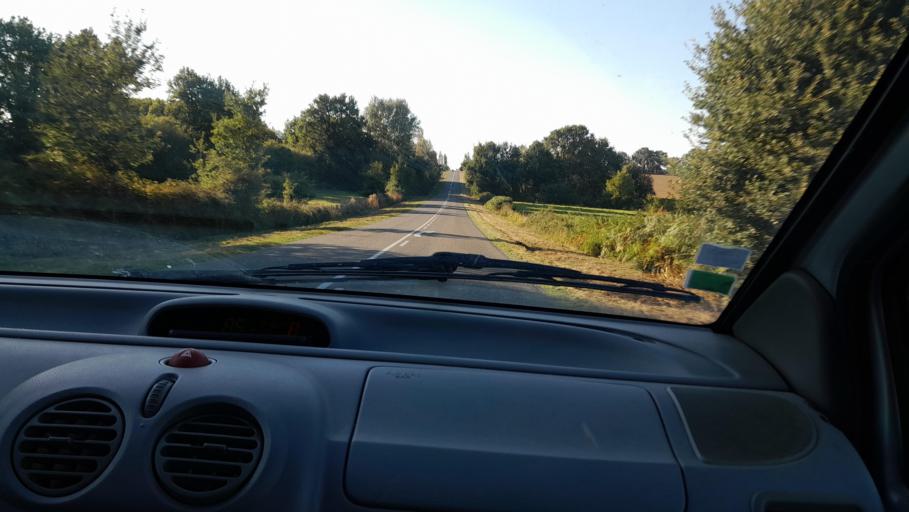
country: FR
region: Pays de la Loire
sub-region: Departement de la Mayenne
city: Craon
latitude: 47.8559
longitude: -0.9689
